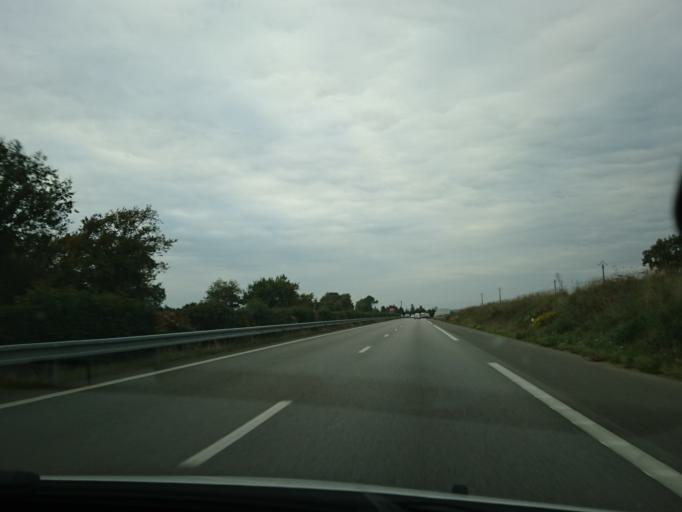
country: FR
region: Brittany
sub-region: Departement du Morbihan
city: Theix
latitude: 47.6199
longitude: -2.6270
